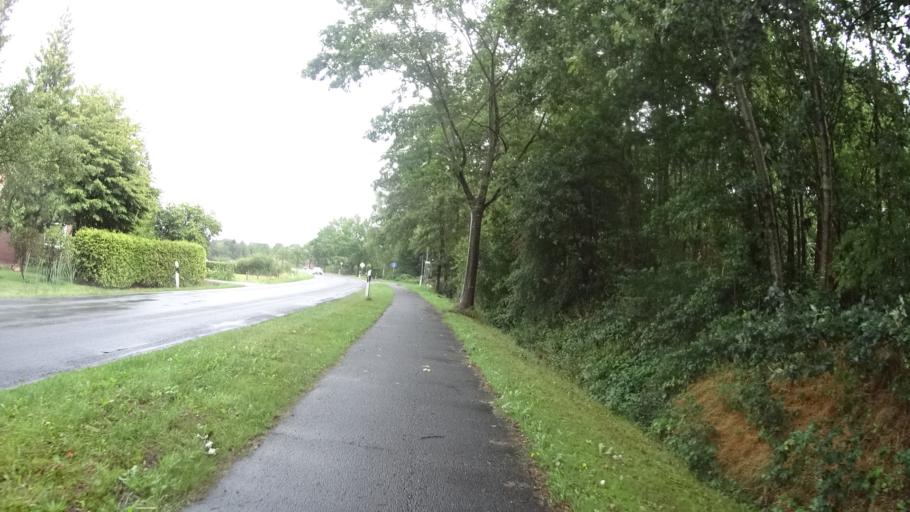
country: DE
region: Lower Saxony
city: Firrel
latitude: 53.3322
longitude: 7.6601
